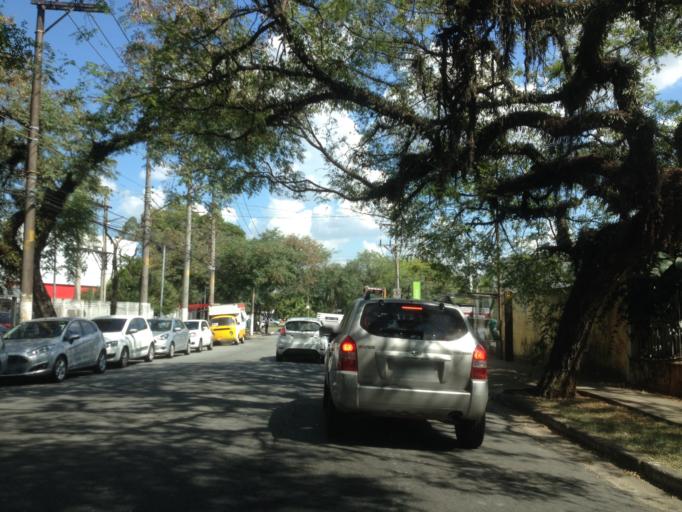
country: BR
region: Sao Paulo
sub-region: Sao Paulo
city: Sao Paulo
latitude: -23.5523
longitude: -46.7080
